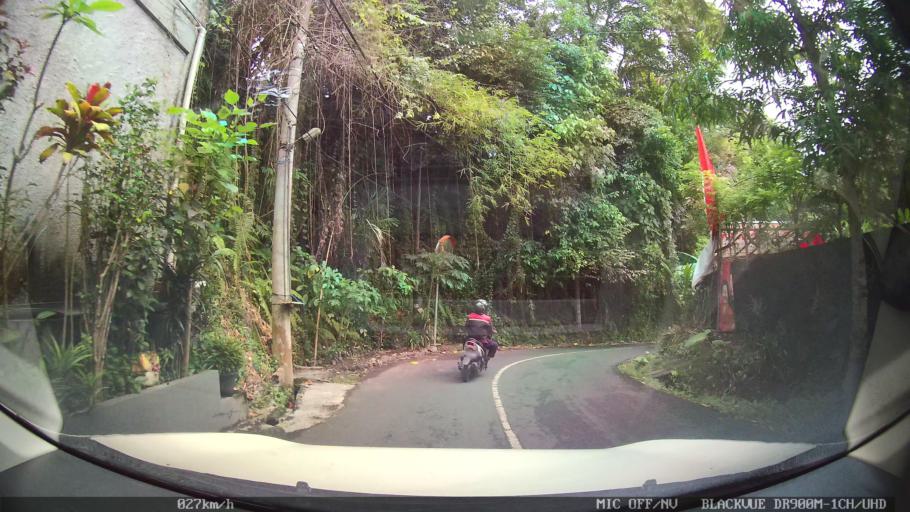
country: ID
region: Bali
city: Banjar Parekan
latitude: -8.5845
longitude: 115.2142
